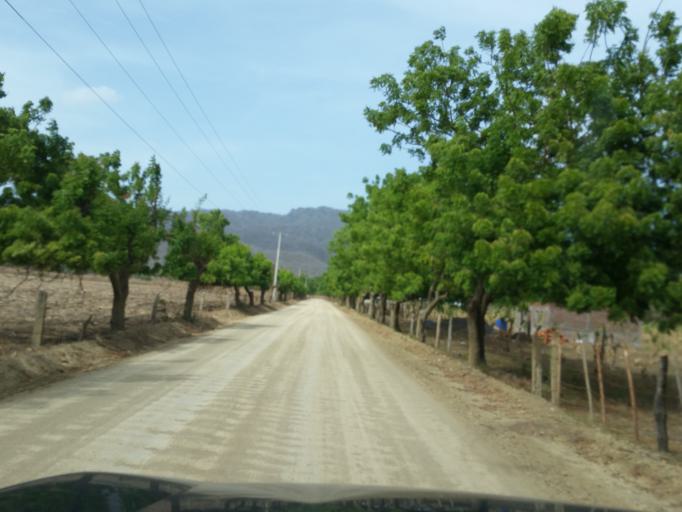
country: NI
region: Rivas
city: Tola
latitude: 11.4259
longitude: -86.0271
